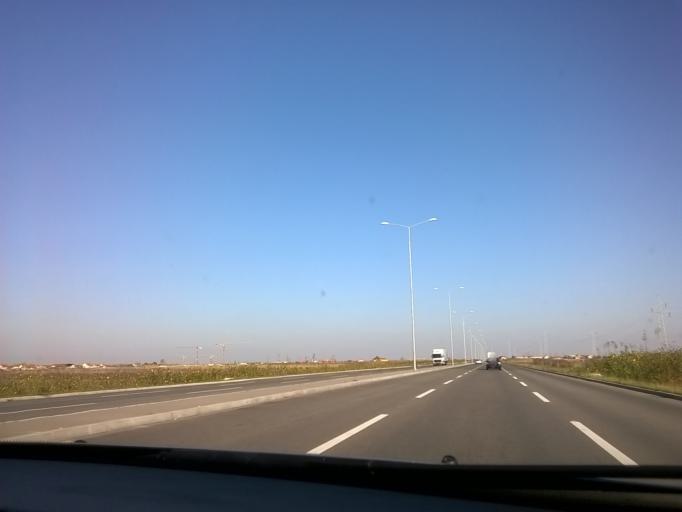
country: RS
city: Ovca
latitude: 44.8751
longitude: 20.5174
